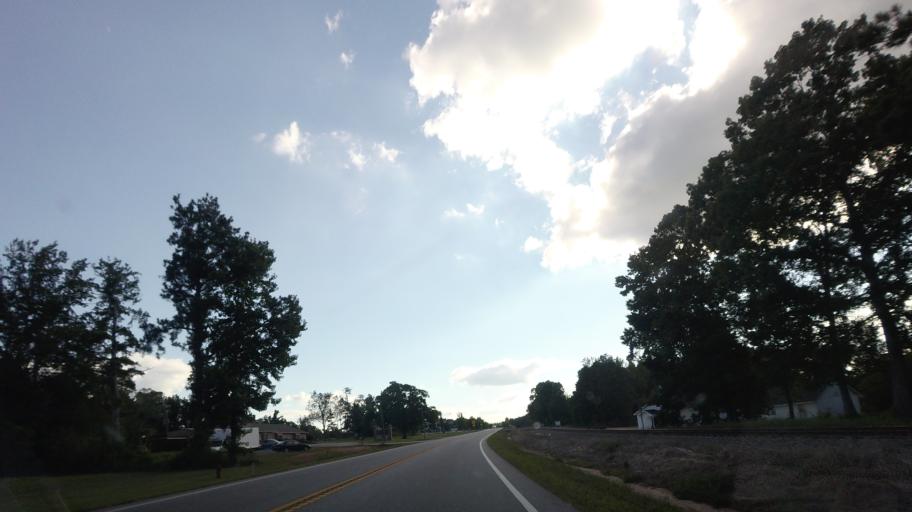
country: US
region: Georgia
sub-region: Lamar County
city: Barnesville
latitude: 33.0033
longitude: -84.1930
